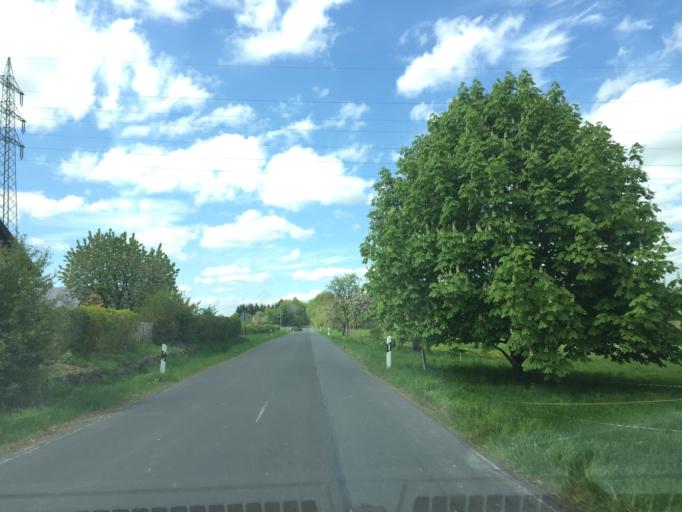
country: DE
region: Rheinland-Pfalz
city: Meudt
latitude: 50.4950
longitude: 7.8934
